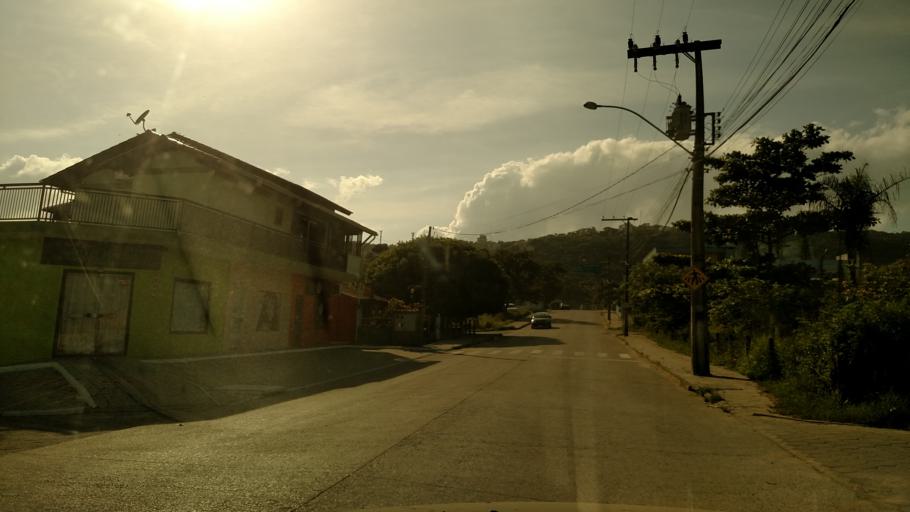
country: BR
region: Santa Catarina
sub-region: Porto Belo
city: Porto Belo
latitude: -27.1530
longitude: -48.5054
